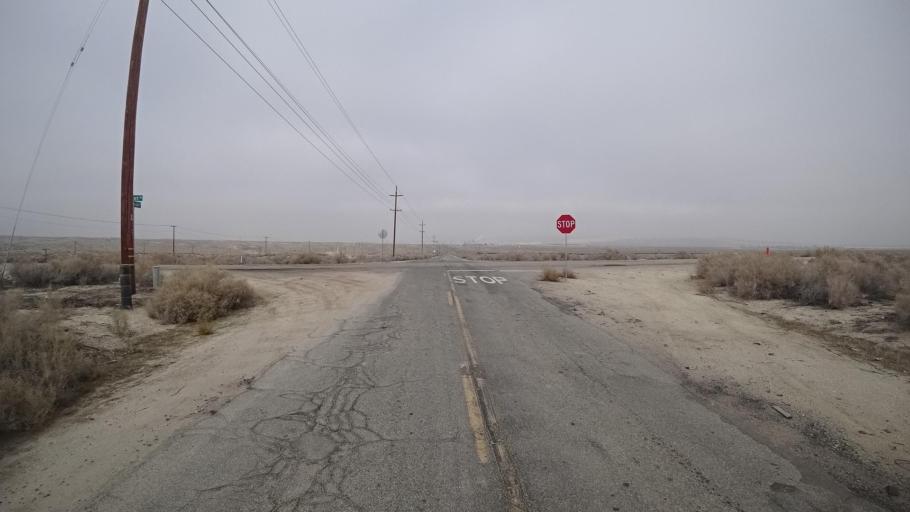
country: US
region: California
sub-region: Kern County
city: Maricopa
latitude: 35.0986
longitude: -119.4023
